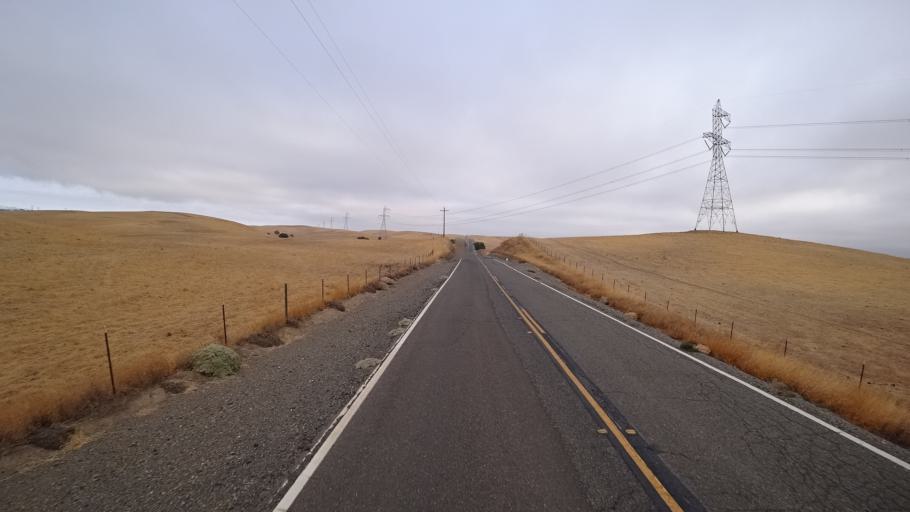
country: US
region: California
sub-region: Yolo County
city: Dunnigan
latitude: 38.8441
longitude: -122.0438
